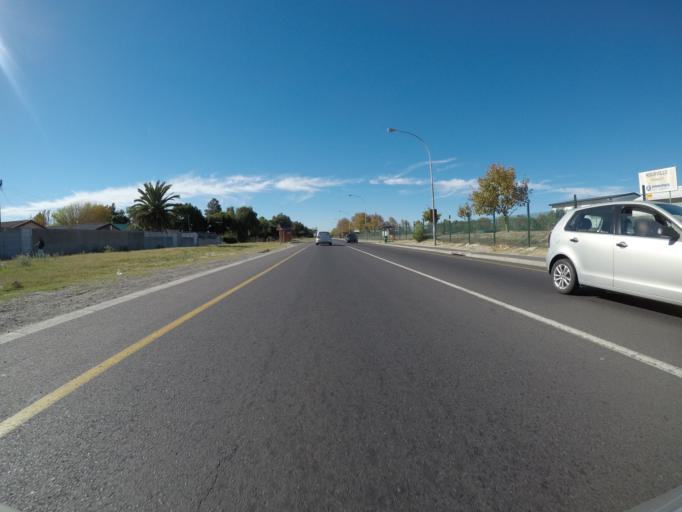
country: ZA
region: Western Cape
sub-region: City of Cape Town
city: Kraaifontein
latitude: -33.9418
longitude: 18.6768
